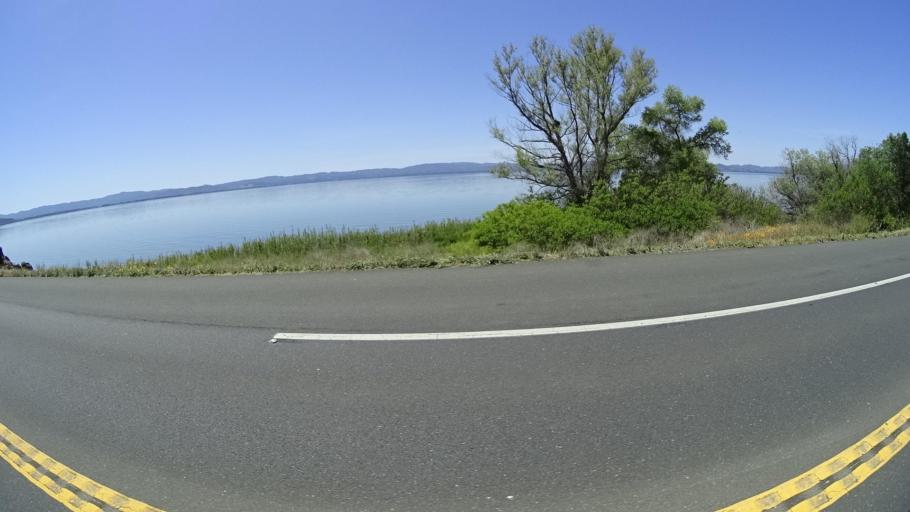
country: US
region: California
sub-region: Lake County
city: Lucerne
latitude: 39.0731
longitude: -122.7825
